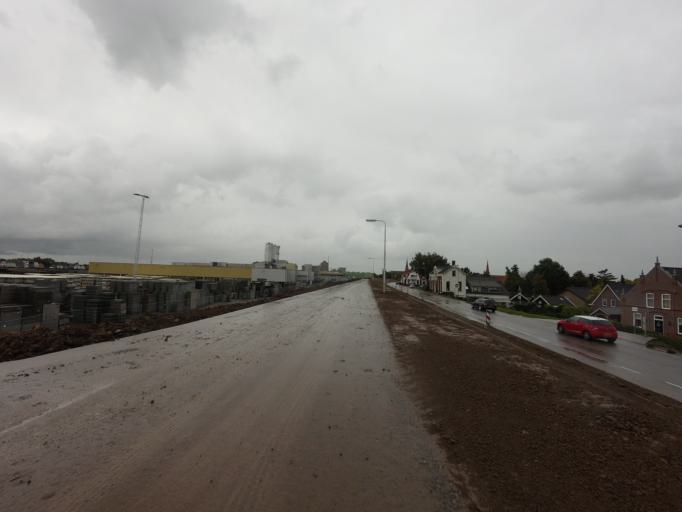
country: NL
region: South Holland
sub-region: Molenwaard
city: Nieuw-Lekkerland
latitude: 51.8907
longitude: 4.6826
